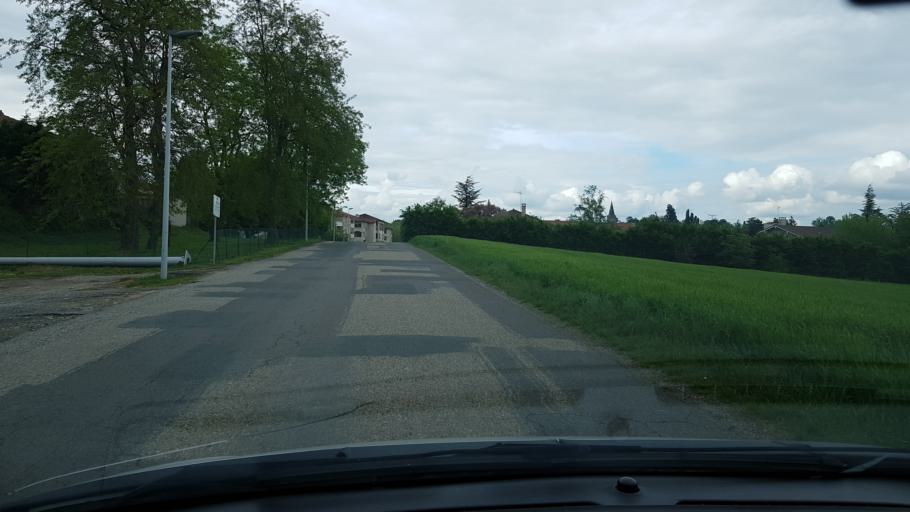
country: FR
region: Rhone-Alpes
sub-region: Departement du Rhone
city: Mornant
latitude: 45.6366
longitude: 4.6859
